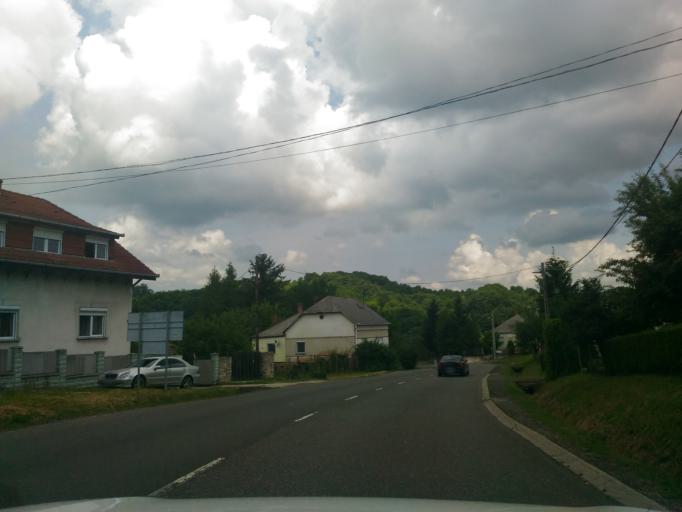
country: HU
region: Baranya
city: Komlo
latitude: 46.1594
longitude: 18.2391
